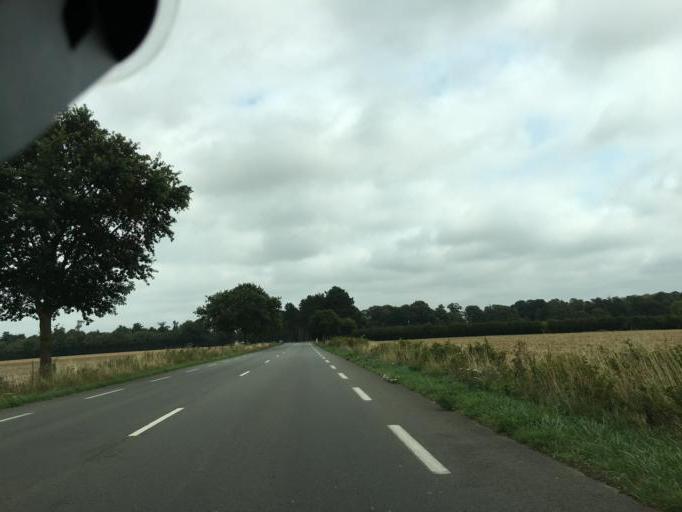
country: FR
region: Nord-Pas-de-Calais
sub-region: Departement du Pas-de-Calais
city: Saint-Pol-sur-Ternoise
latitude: 50.4078
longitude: 2.3700
